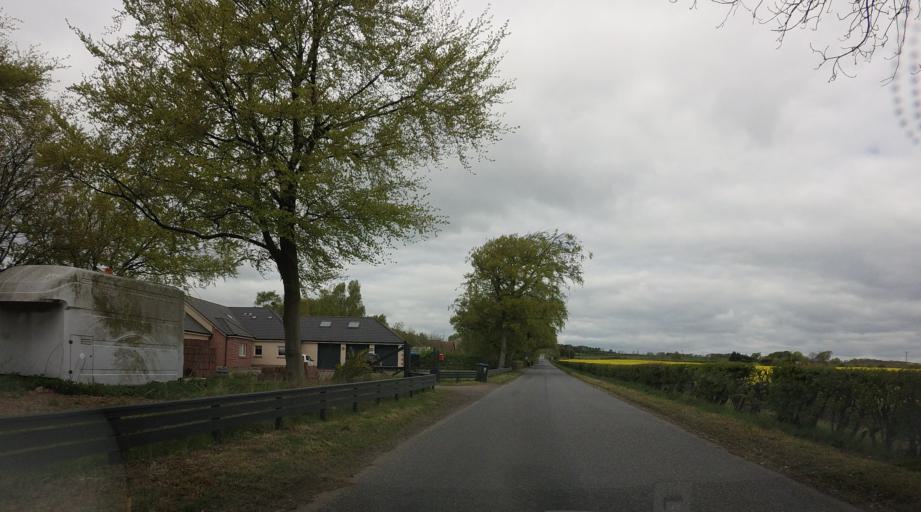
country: GB
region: Scotland
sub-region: Perth and Kinross
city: Milnathort
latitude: 56.2419
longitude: -3.3722
